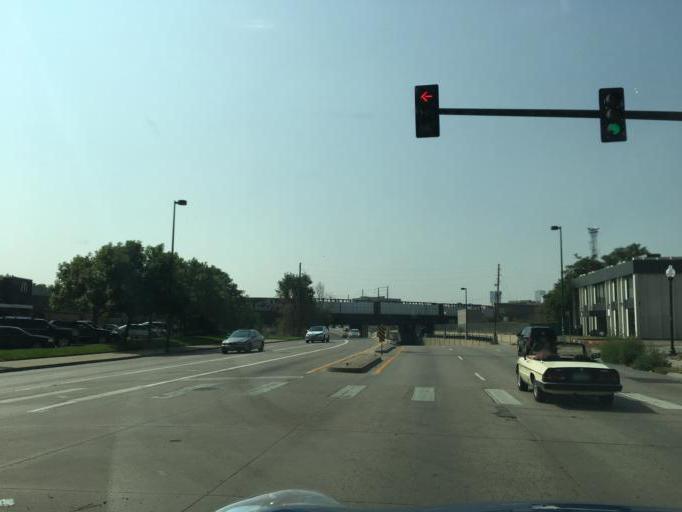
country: US
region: Colorado
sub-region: Denver County
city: Denver
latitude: 39.7785
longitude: -104.9793
